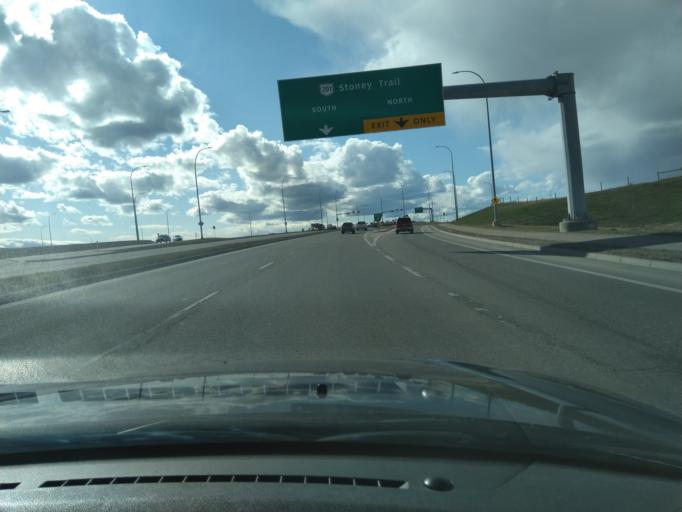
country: CA
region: Alberta
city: Calgary
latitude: 51.1431
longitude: -114.1984
